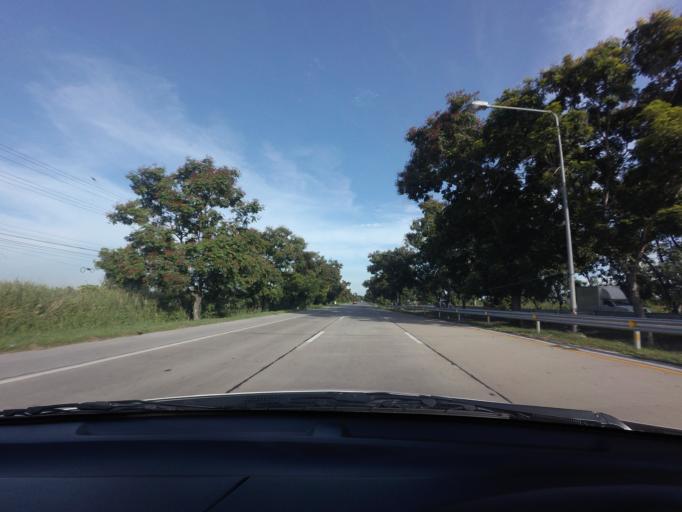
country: TH
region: Phra Nakhon Si Ayutthaya
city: Lat Bua Luang
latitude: 14.2149
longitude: 100.2838
